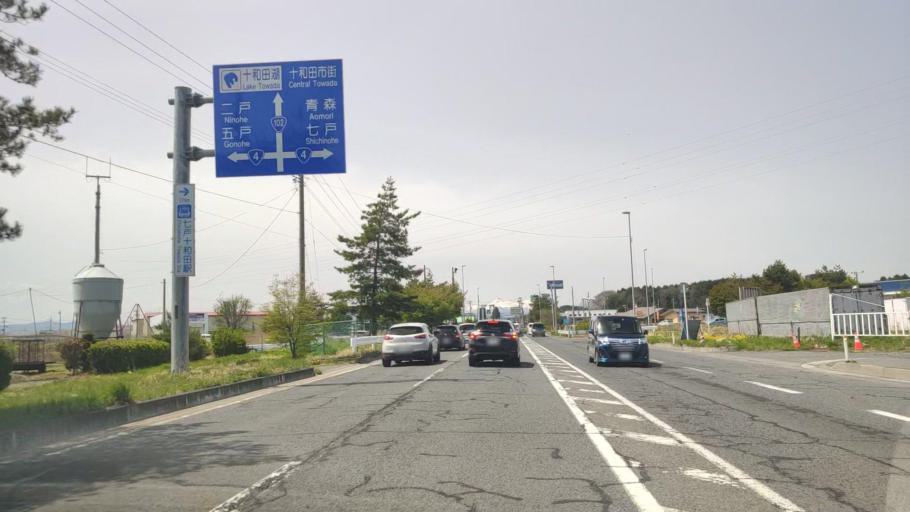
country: JP
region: Aomori
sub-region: Misawa Shi
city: Inuotose
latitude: 40.6122
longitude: 141.2620
